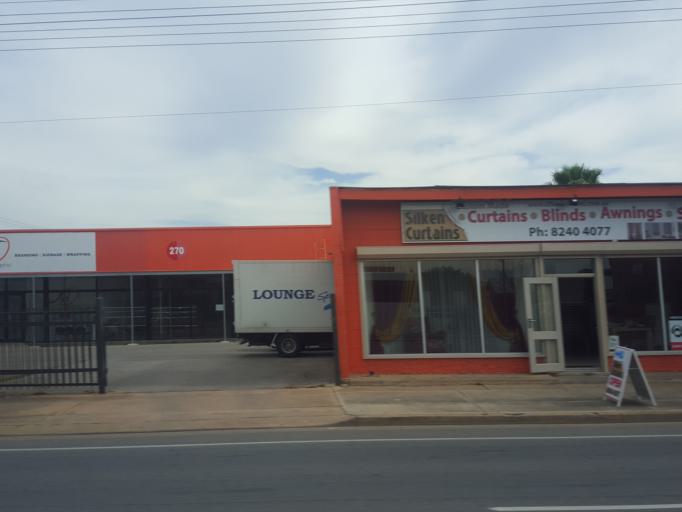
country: AU
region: South Australia
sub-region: Charles Sturt
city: Woodville North
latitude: -34.8507
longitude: 138.5438
